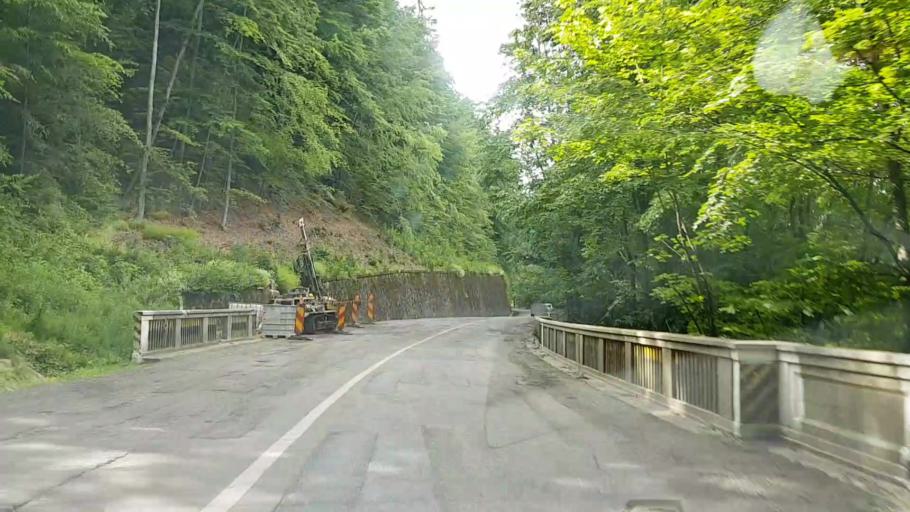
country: RO
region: Neamt
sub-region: Comuna Bicaz
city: Dodeni
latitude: 46.9368
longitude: 26.1190
